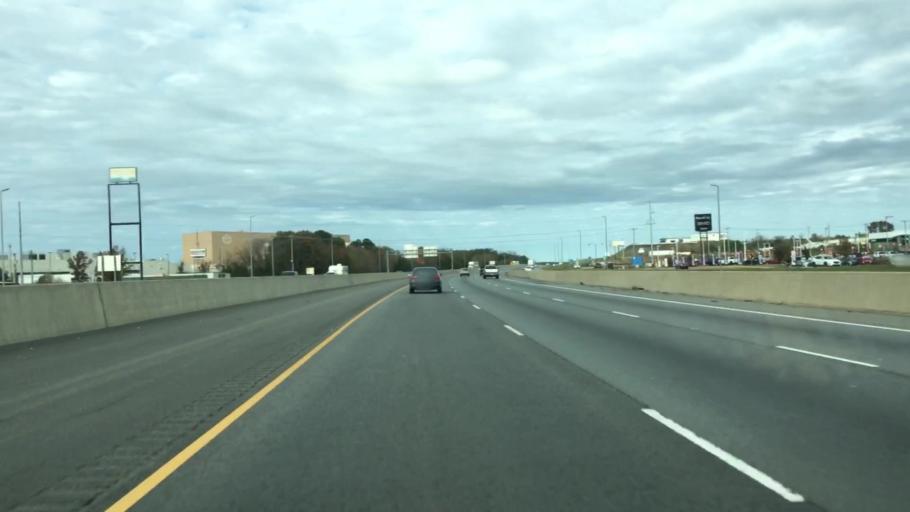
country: US
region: Arkansas
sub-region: Faulkner County
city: Conway
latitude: 35.0683
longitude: -92.4176
